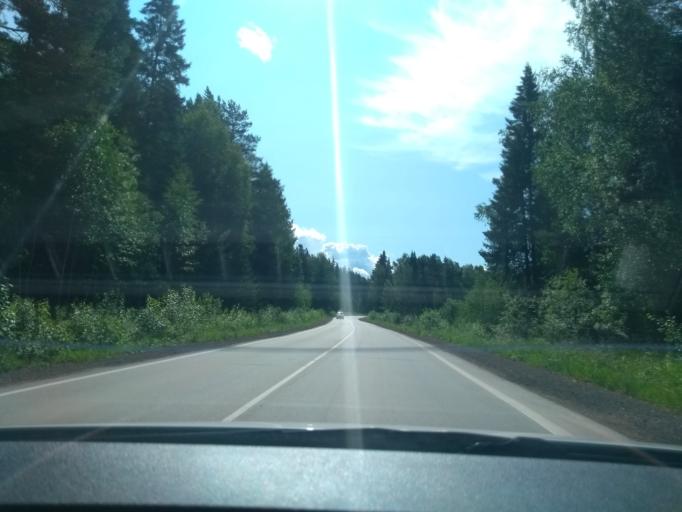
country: RU
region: Perm
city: Lobanovo
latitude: 57.8337
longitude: 56.4016
